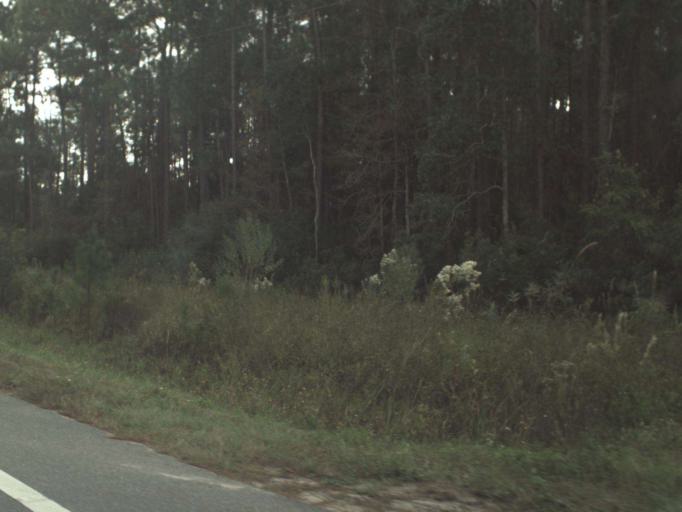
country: US
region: Florida
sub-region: Wakulla County
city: Crawfordville
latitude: 30.0023
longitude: -84.5040
